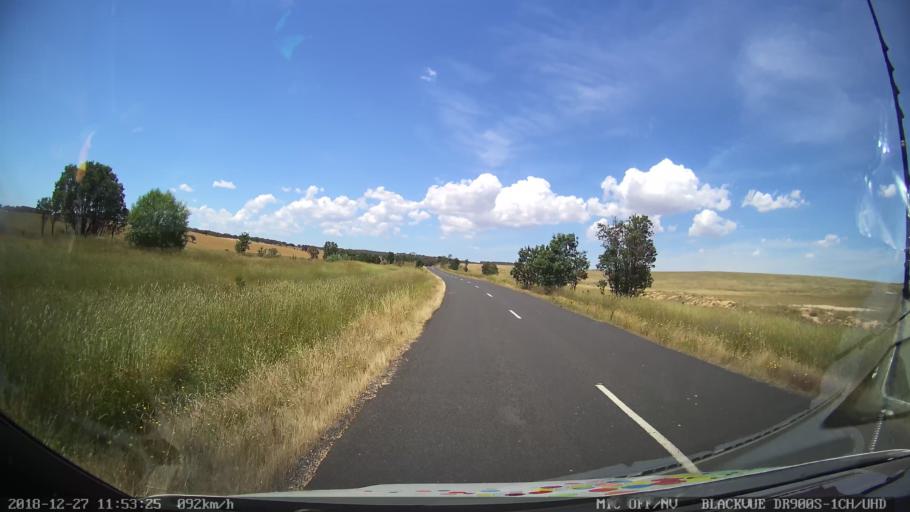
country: AU
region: New South Wales
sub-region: Blayney
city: Blayney
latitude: -33.6616
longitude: 149.4014
